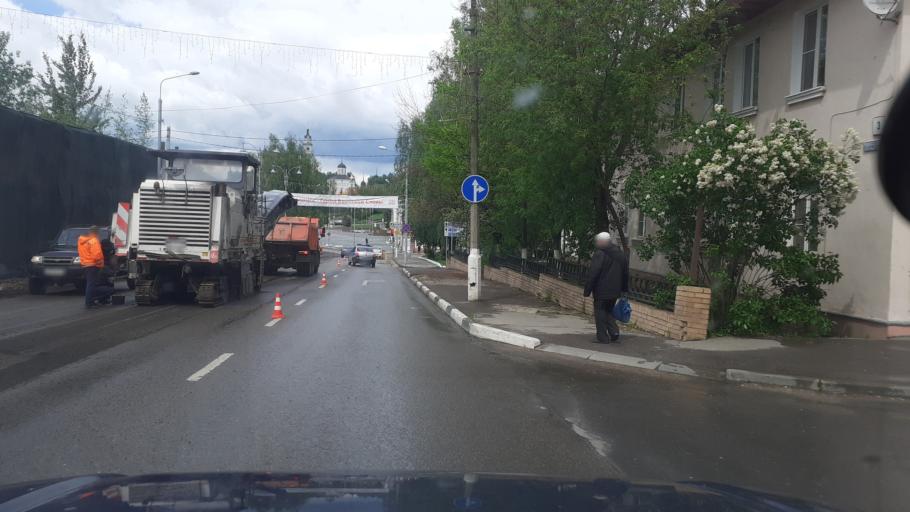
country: RU
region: Moskovskaya
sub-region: Volokolamskiy Rayon
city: Volokolamsk
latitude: 56.0335
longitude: 35.9592
